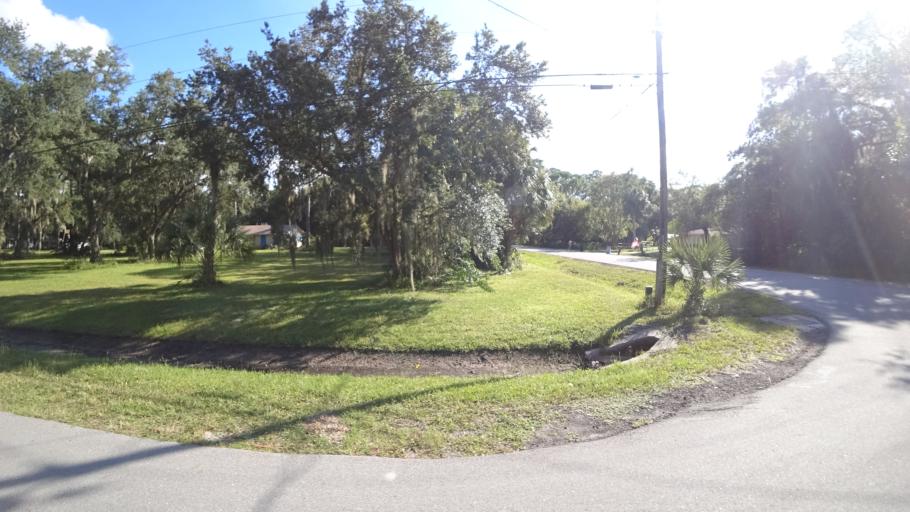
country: US
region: Florida
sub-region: Manatee County
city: Samoset
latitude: 27.4669
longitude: -82.4739
